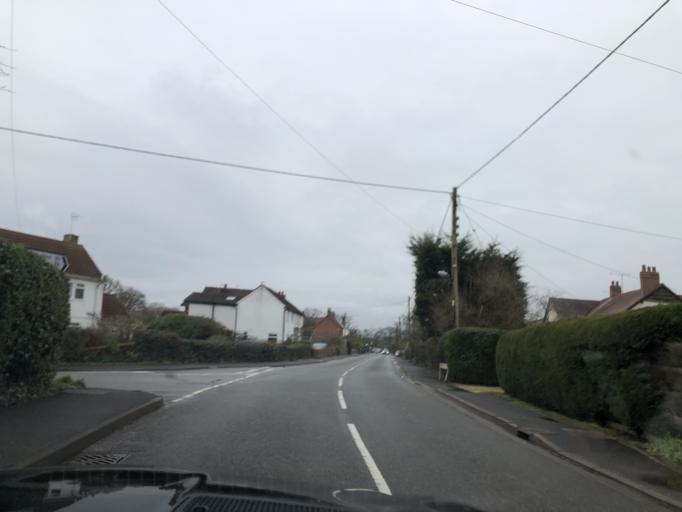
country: GB
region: England
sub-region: Warwickshire
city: Wroxall
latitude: 52.3051
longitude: -1.6853
